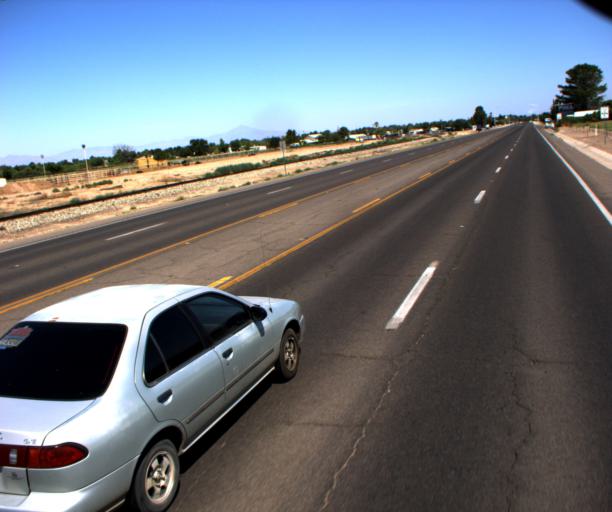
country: US
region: Arizona
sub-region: Graham County
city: Pima
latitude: 32.8879
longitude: -109.8151
